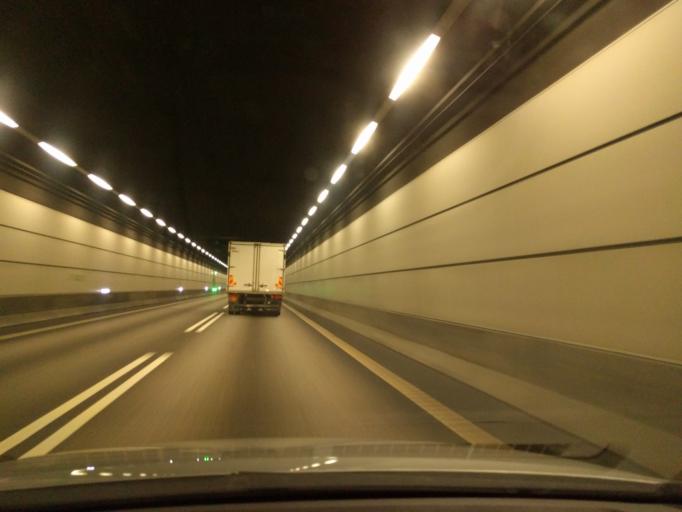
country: DK
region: Capital Region
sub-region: Dragor Kommune
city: Dragor
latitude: 55.6227
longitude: 12.6983
